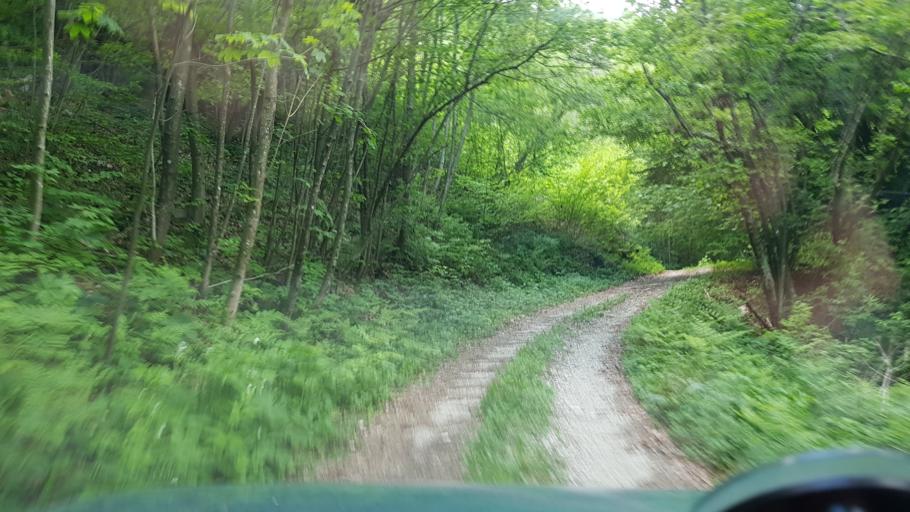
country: IT
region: Friuli Venezia Giulia
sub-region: Provincia di Udine
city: Torreano
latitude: 46.1862
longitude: 13.4224
